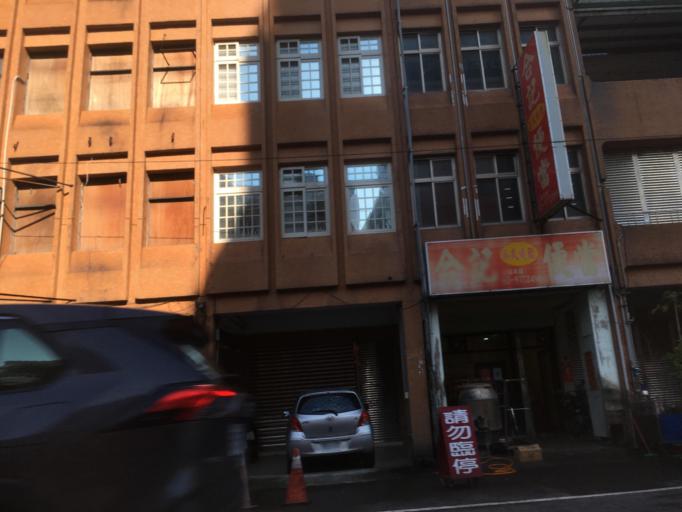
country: TW
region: Taiwan
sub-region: Yilan
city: Yilan
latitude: 24.8564
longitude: 121.8244
